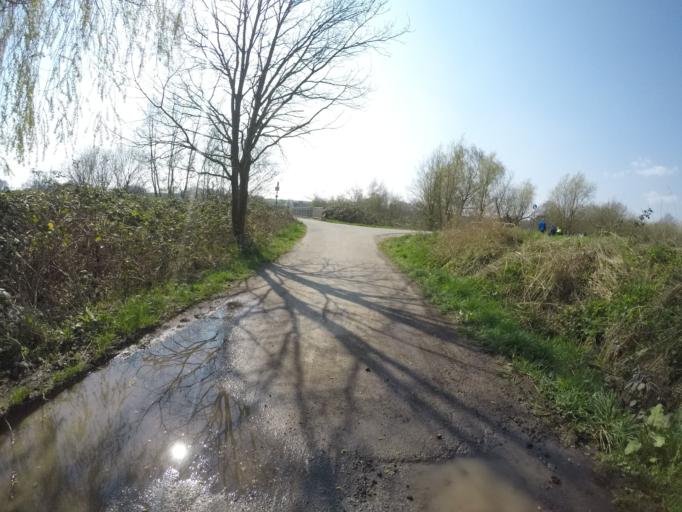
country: DE
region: North Rhine-Westphalia
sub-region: Regierungsbezirk Detmold
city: Bielefeld
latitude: 52.0556
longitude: 8.5740
